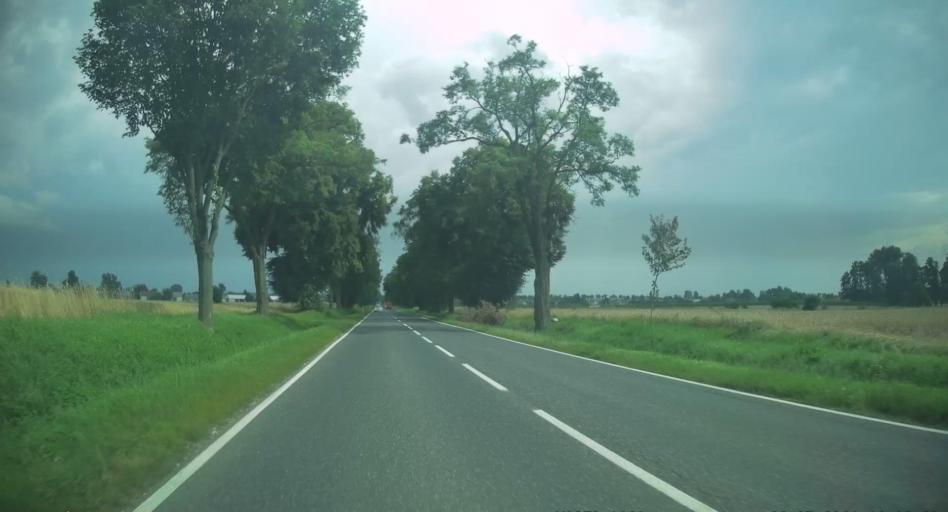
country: PL
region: Lodz Voivodeship
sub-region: Powiat skierniewicki
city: Gluchow
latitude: 51.7849
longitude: 20.0544
